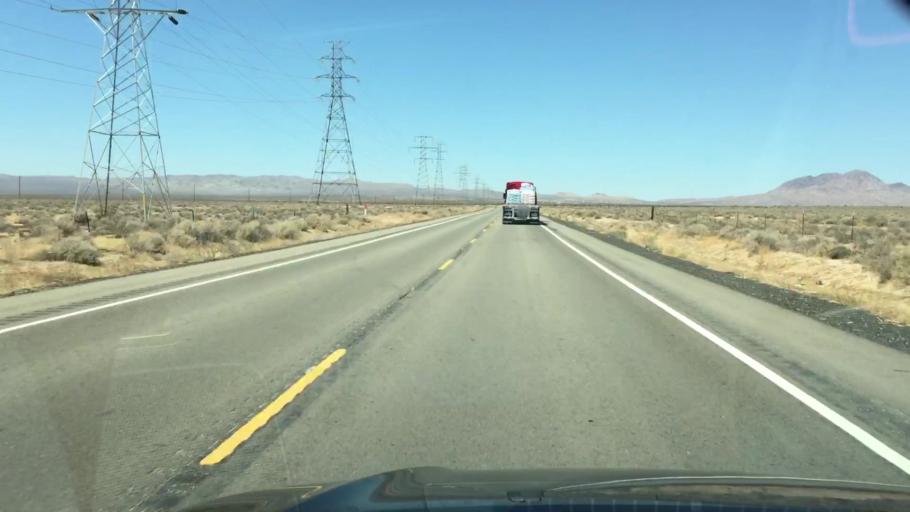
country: US
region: California
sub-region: Kern County
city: Boron
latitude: 35.2132
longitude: -117.6031
